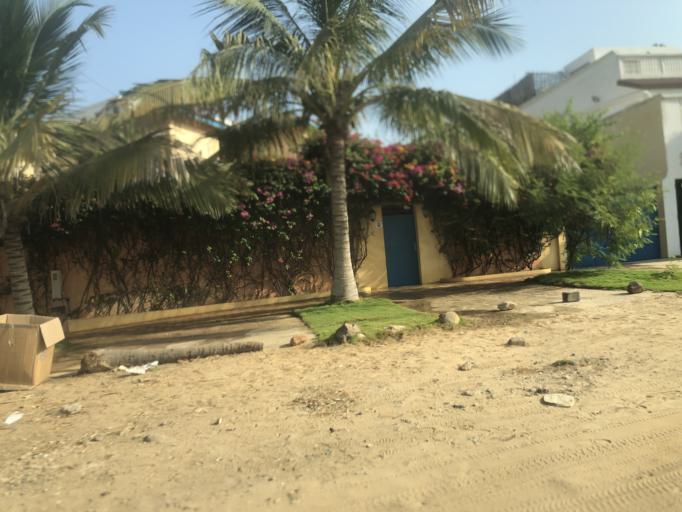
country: SN
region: Dakar
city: Mermoz Boabab
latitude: 14.7401
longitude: -17.5118
